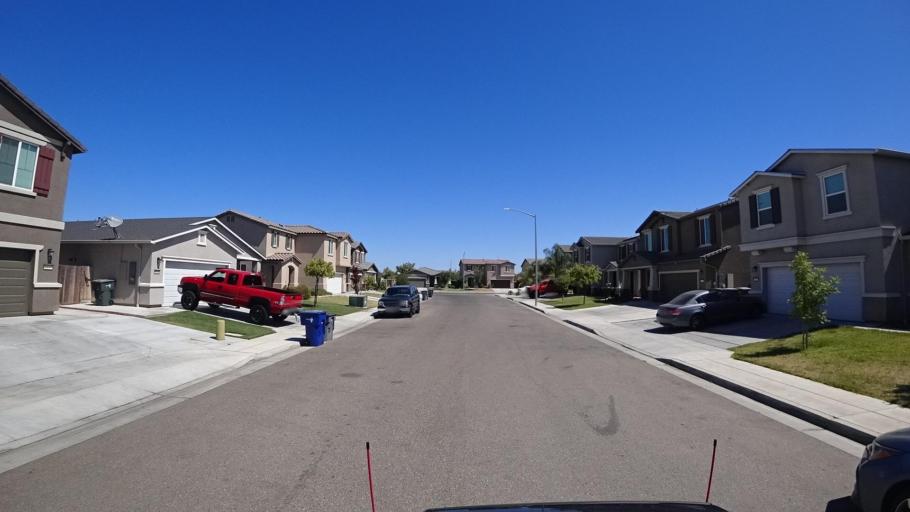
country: US
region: California
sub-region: Fresno County
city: Sunnyside
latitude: 36.7195
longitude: -119.6708
